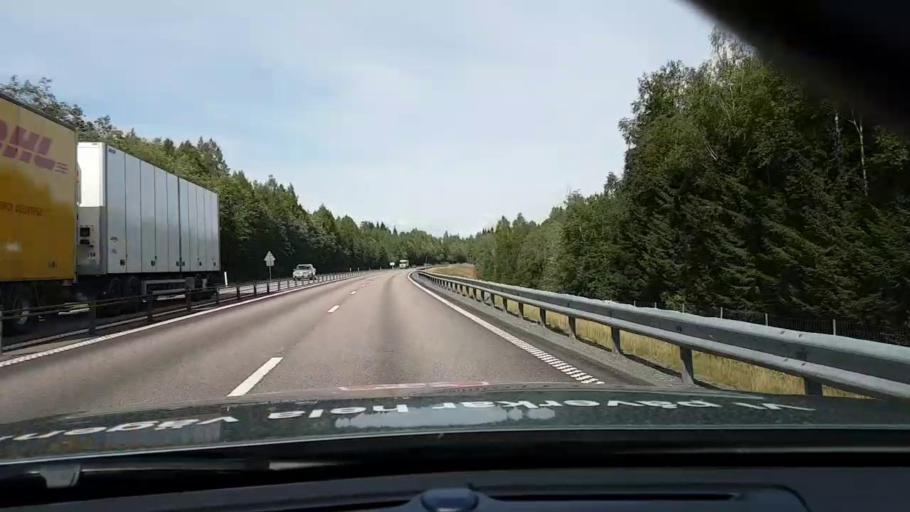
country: SE
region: Vaesternorrland
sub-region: OErnskoeldsviks Kommun
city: Husum
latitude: 63.4212
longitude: 19.2049
